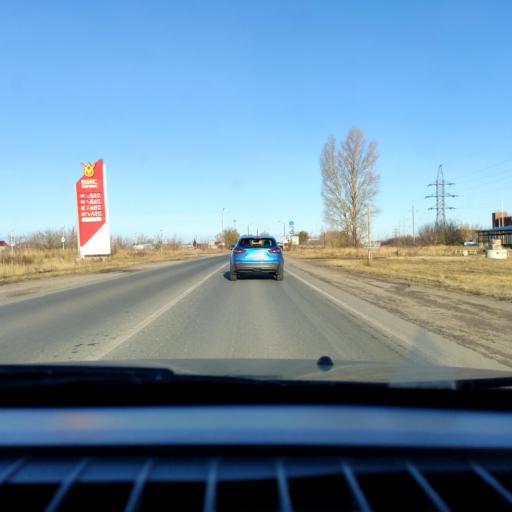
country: RU
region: Samara
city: Tol'yatti
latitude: 53.5718
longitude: 49.3420
